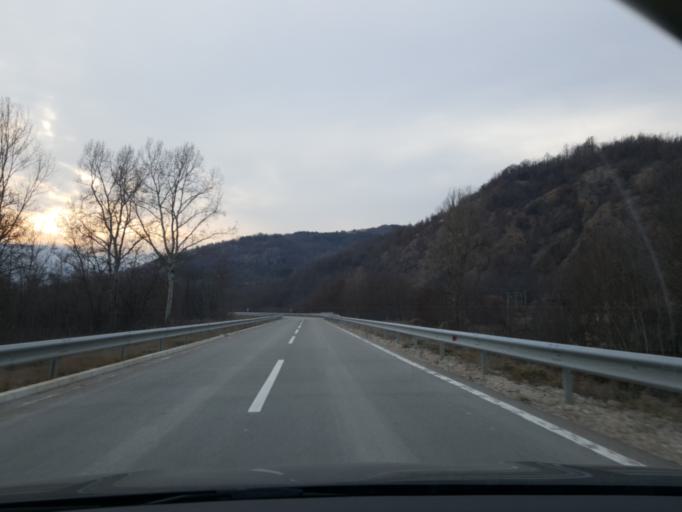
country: RS
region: Central Serbia
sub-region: Pirotski Okrug
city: Bela Palanka
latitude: 43.2382
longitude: 22.4045
